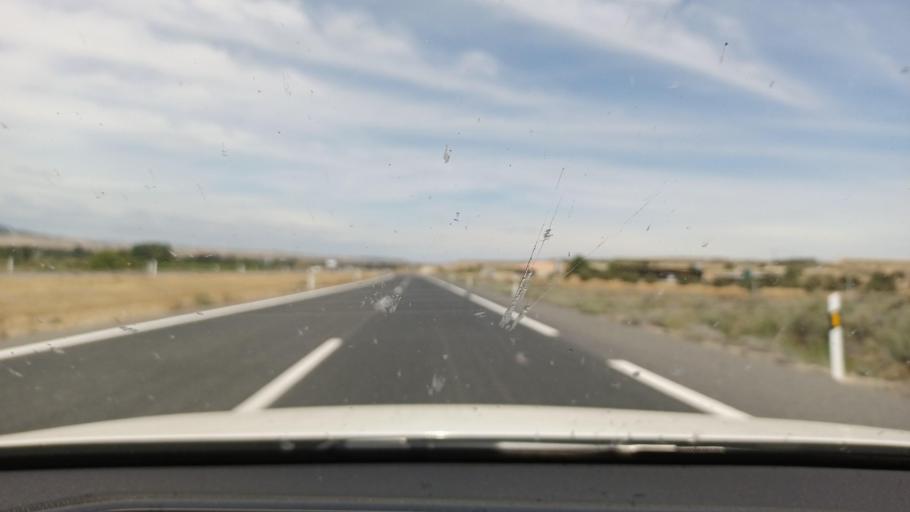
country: ES
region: Aragon
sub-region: Provincia de Zaragoza
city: Mallen
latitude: 41.8843
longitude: -1.4108
